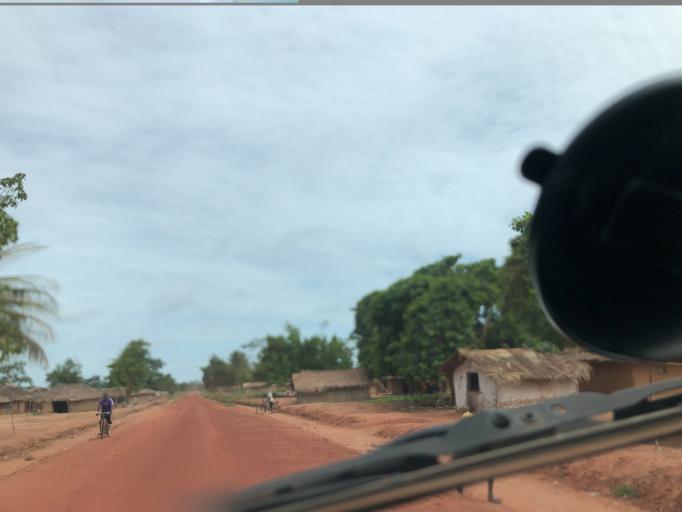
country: CD
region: Equateur
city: Gemena
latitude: 3.2903
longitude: 19.5168
